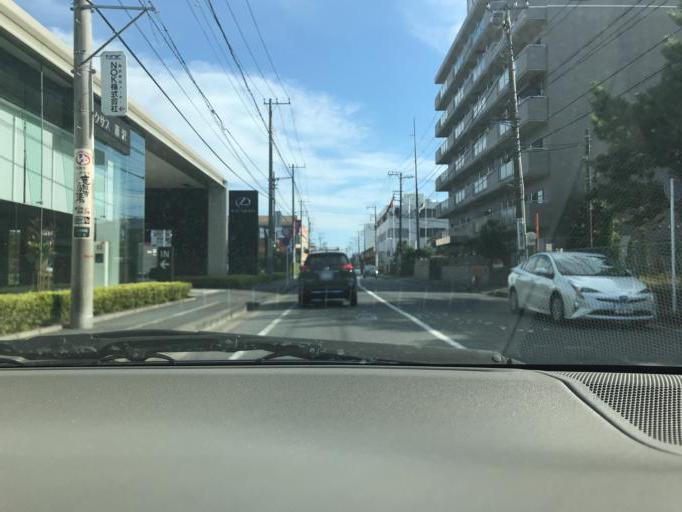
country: JP
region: Kanagawa
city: Fujisawa
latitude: 35.3411
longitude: 139.4628
